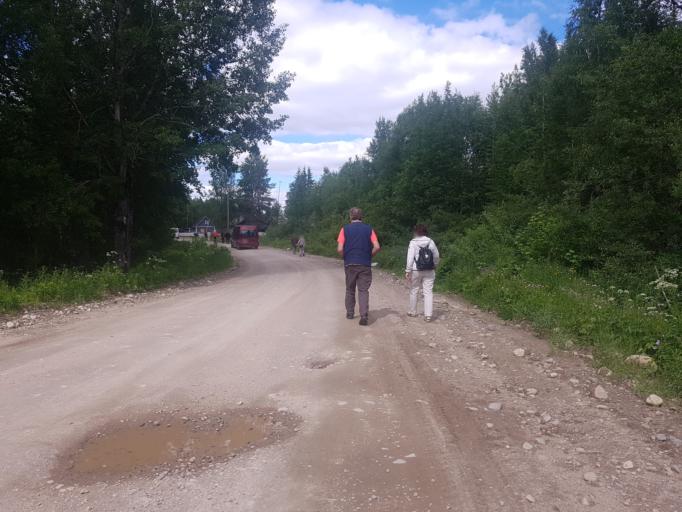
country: RU
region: Republic of Karelia
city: Kostomuksha
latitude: 65.1854
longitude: 30.2901
